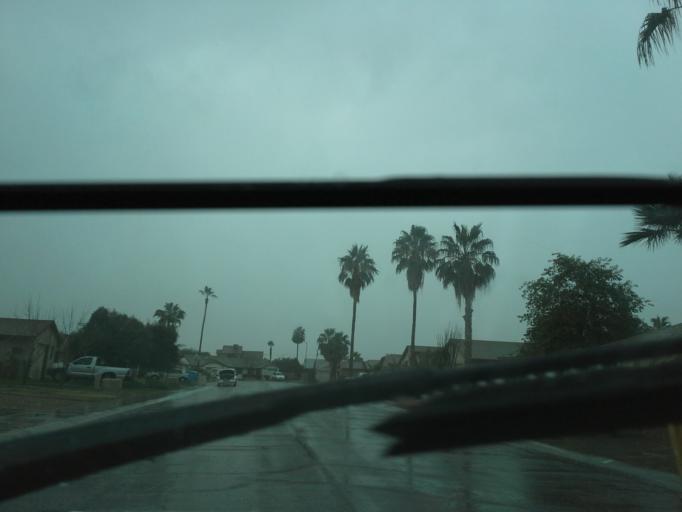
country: US
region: Arizona
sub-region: Maricopa County
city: Paradise Valley
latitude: 33.6339
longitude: -112.0458
